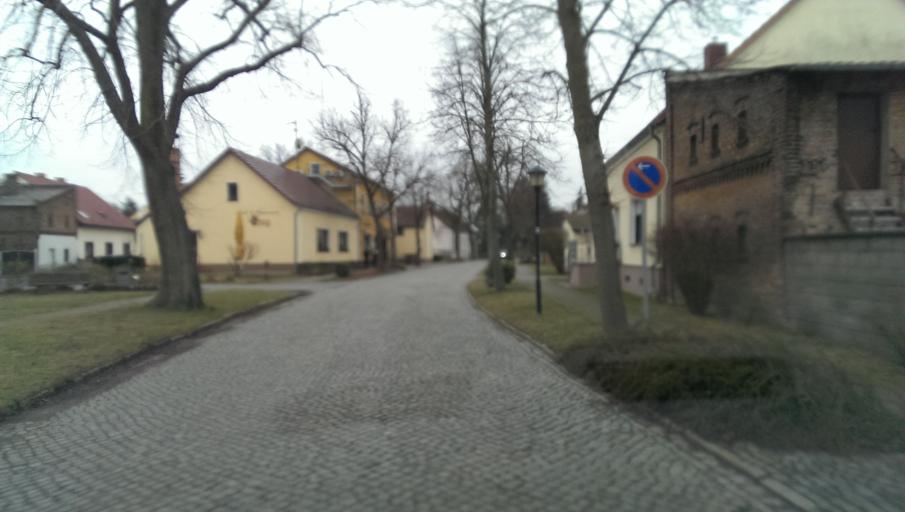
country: DE
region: Brandenburg
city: Mittenwalde
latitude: 52.2135
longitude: 13.5579
